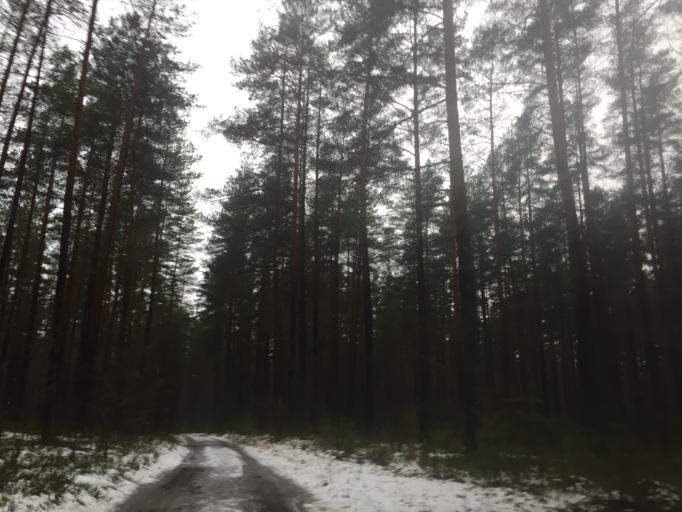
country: LV
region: Stopini
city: Ulbroka
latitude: 56.9518
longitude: 24.3437
